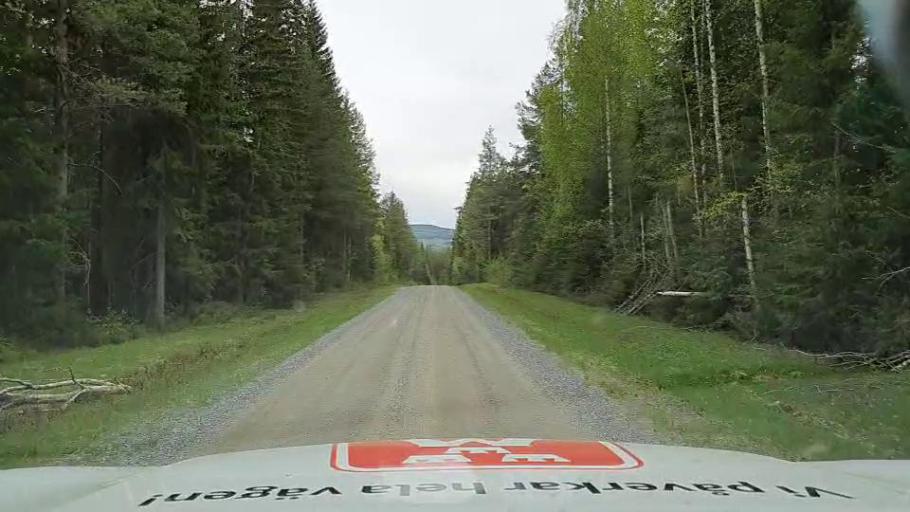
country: SE
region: Jaemtland
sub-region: Bergs Kommun
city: Hoverberg
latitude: 62.5170
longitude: 14.7073
